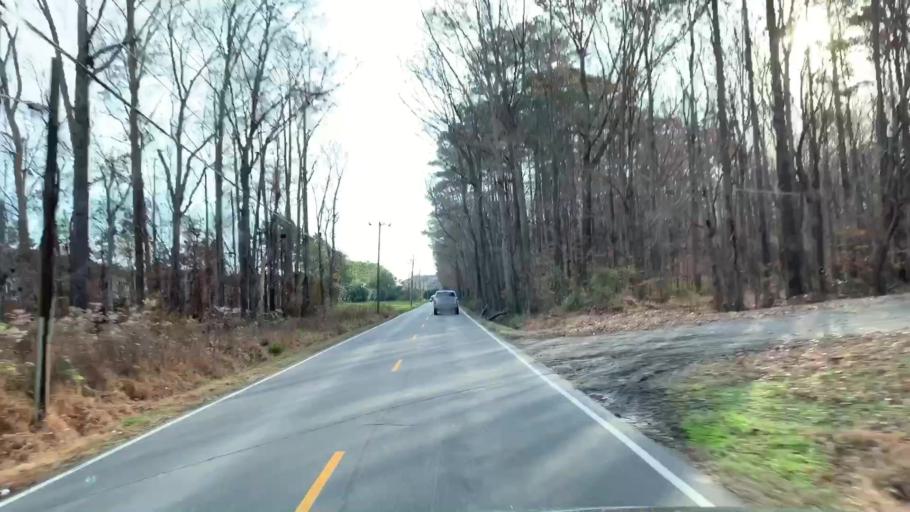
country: US
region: Virginia
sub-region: City of Virginia Beach
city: Virginia Beach
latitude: 36.7255
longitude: -76.0728
